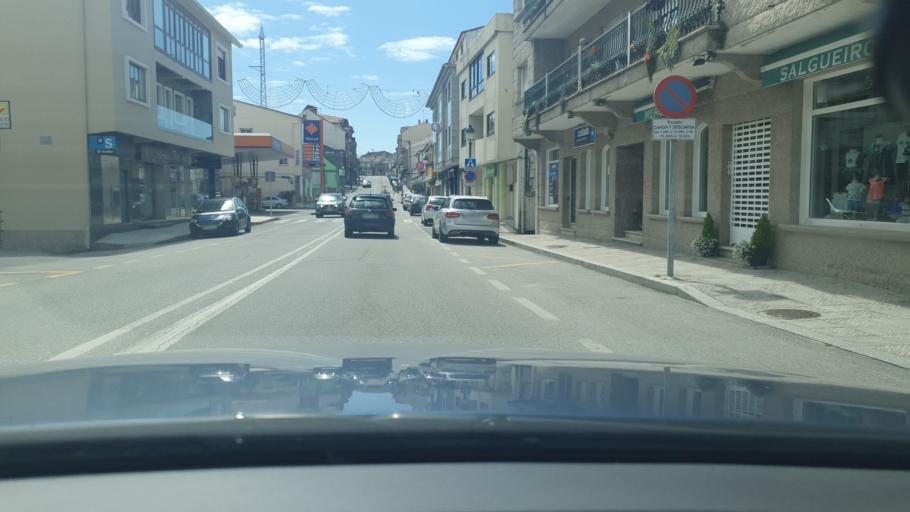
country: ES
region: Galicia
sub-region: Provincia de Pontevedra
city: Sanxenxo
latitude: 42.4435
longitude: -8.8319
